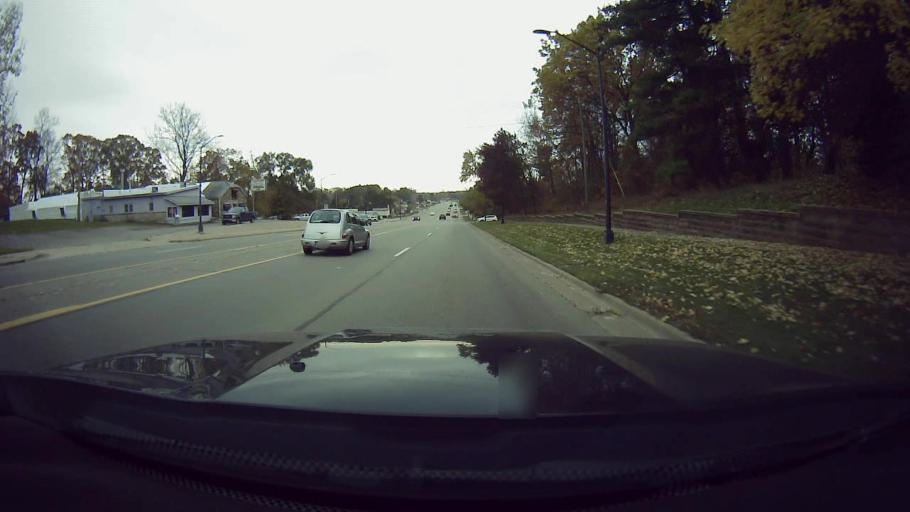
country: US
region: Michigan
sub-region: Oakland County
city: Waterford
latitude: 42.7087
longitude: -83.4063
